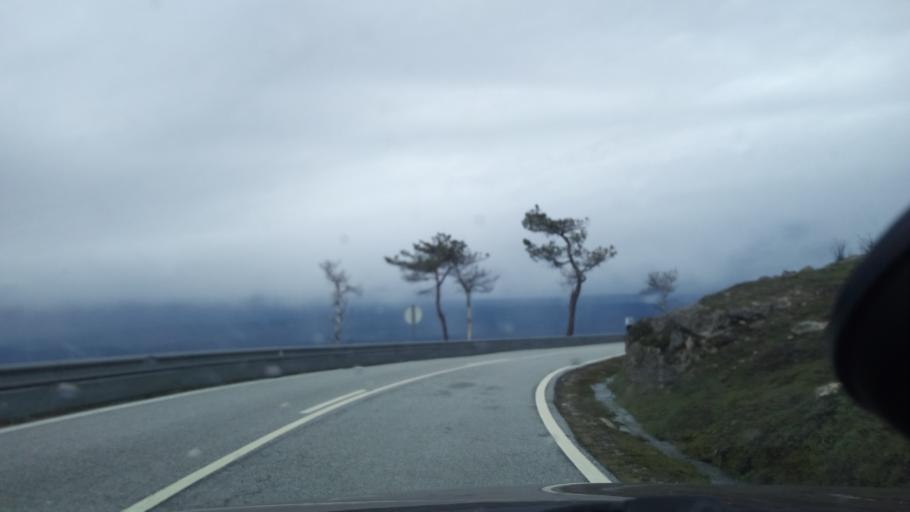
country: PT
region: Guarda
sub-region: Manteigas
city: Manteigas
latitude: 40.4512
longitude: -7.6002
